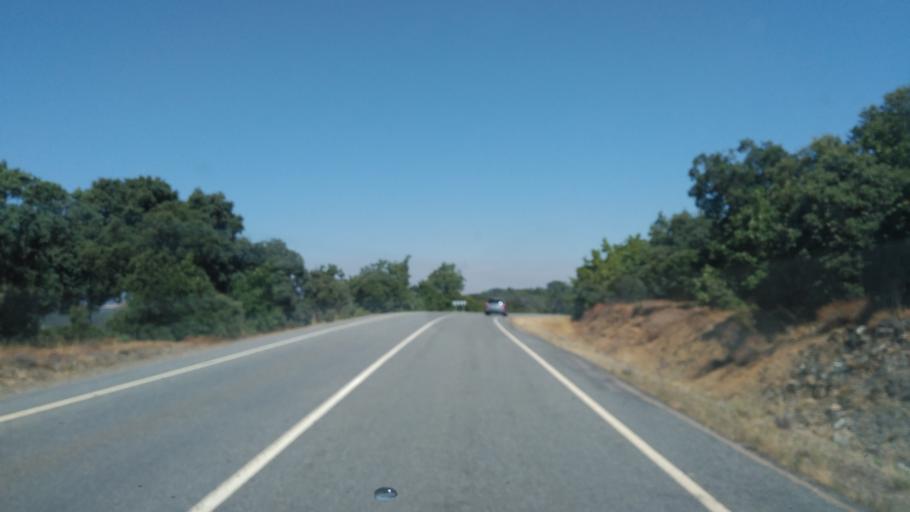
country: ES
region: Castille and Leon
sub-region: Provincia de Salamanca
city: Aldeanueva de la Sierra
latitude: 40.5991
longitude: -6.0936
